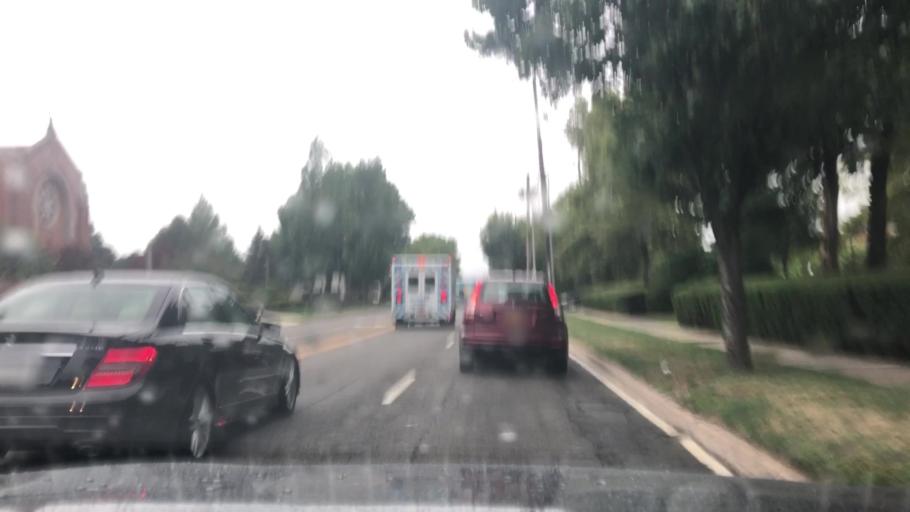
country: US
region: New York
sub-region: Nassau County
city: Garden City
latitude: 40.7215
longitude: -73.6325
